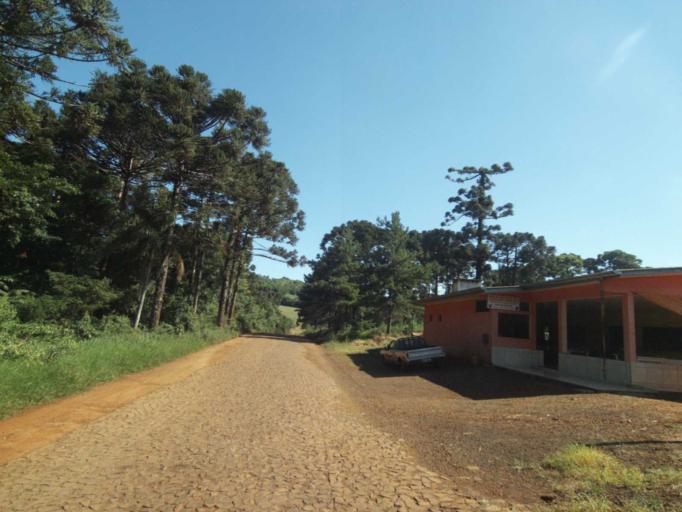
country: BR
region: Parana
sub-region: Laranjeiras Do Sul
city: Laranjeiras do Sul
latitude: -25.3849
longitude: -52.2022
